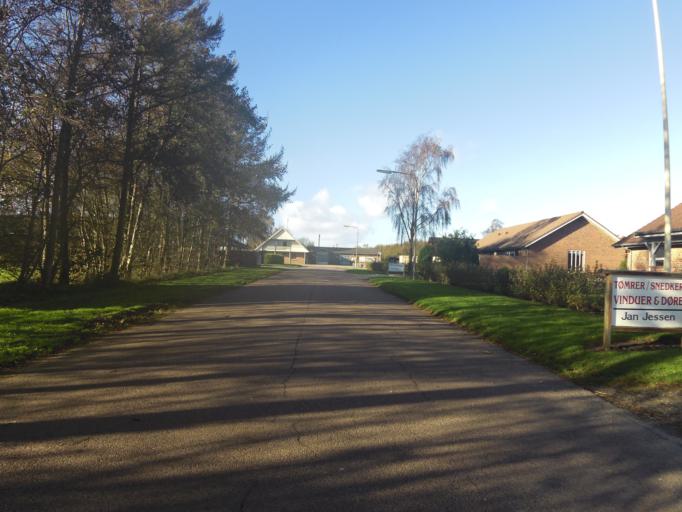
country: DK
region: South Denmark
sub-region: Tonder Kommune
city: Sherrebek
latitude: 55.1529
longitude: 8.7787
